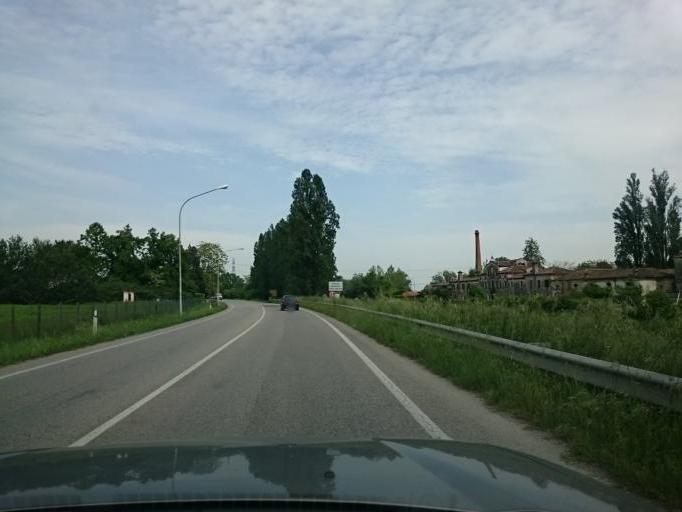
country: IT
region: Veneto
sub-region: Provincia di Venezia
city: Dolo
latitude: 45.4262
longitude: 12.0993
